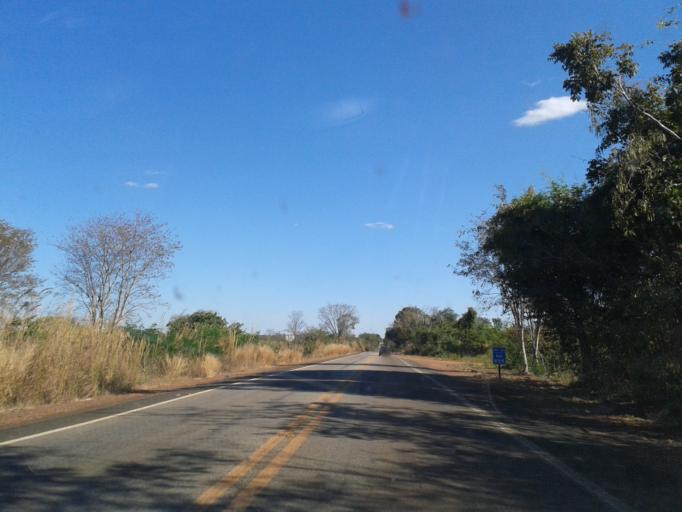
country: BR
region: Goias
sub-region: Mozarlandia
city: Mozarlandia
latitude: -14.6804
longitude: -50.5385
